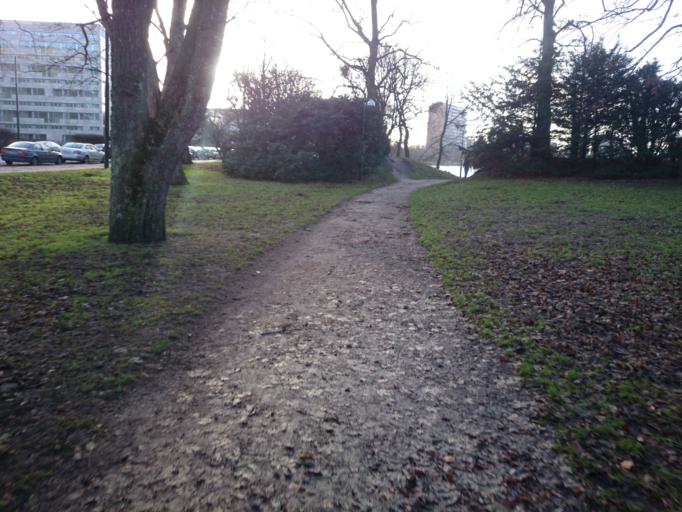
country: SE
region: Skane
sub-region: Malmo
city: Malmoe
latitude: 55.5902
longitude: 12.9976
